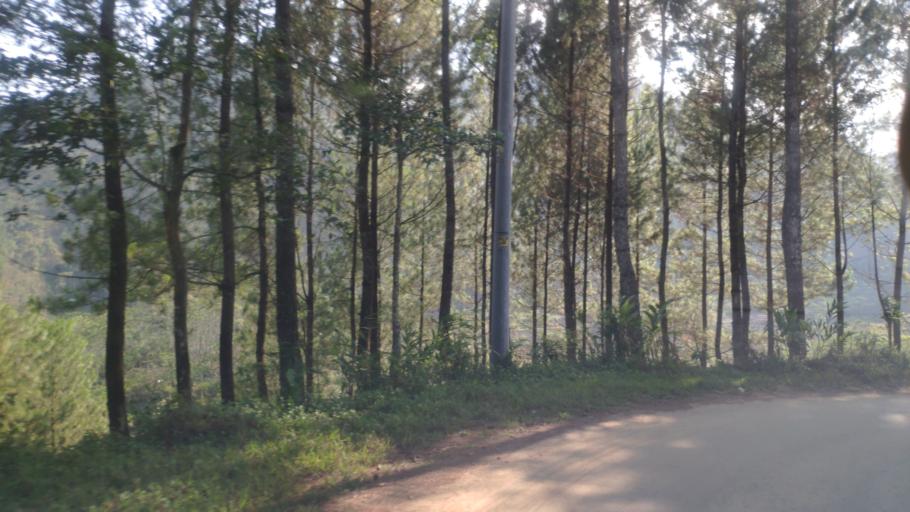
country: ID
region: Central Java
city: Buaran
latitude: -7.2440
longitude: 109.5923
